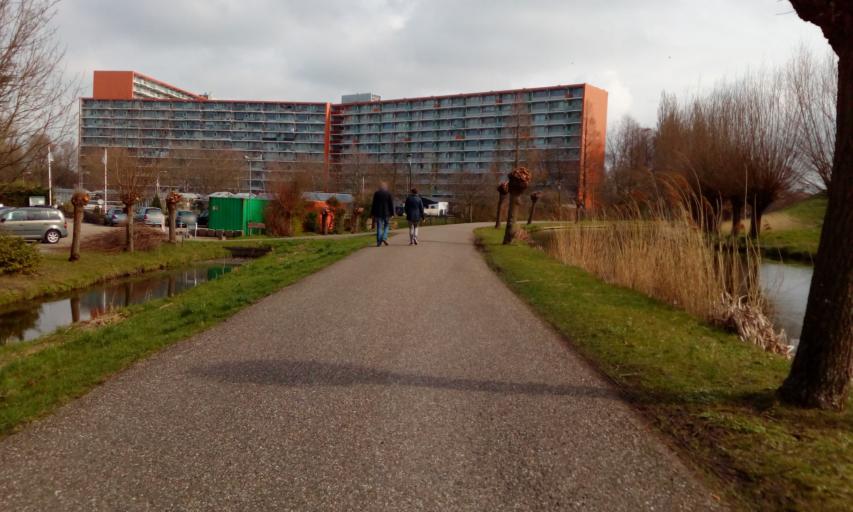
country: NL
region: South Holland
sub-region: Gemeente Maassluis
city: Maassluis
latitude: 51.9307
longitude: 4.2454
